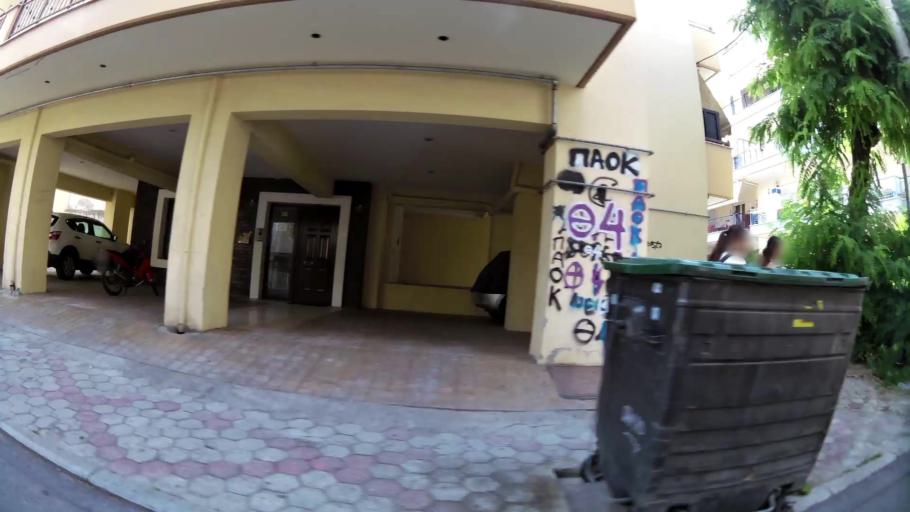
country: GR
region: Central Macedonia
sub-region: Nomos Thessalonikis
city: Sykies
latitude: 40.6491
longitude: 22.9508
